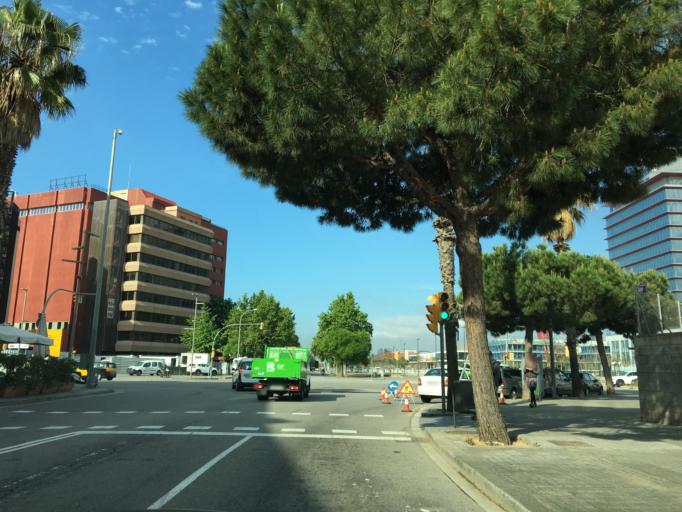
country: ES
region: Catalonia
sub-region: Provincia de Barcelona
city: Sants-Montjuic
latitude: 41.3566
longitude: 2.1423
